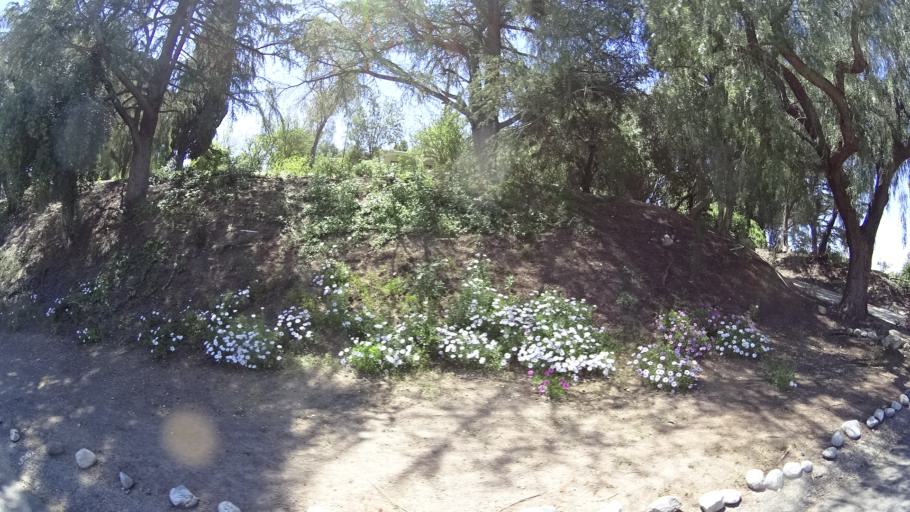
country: US
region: California
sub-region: Ventura County
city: Thousand Oaks
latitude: 34.1870
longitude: -118.8504
